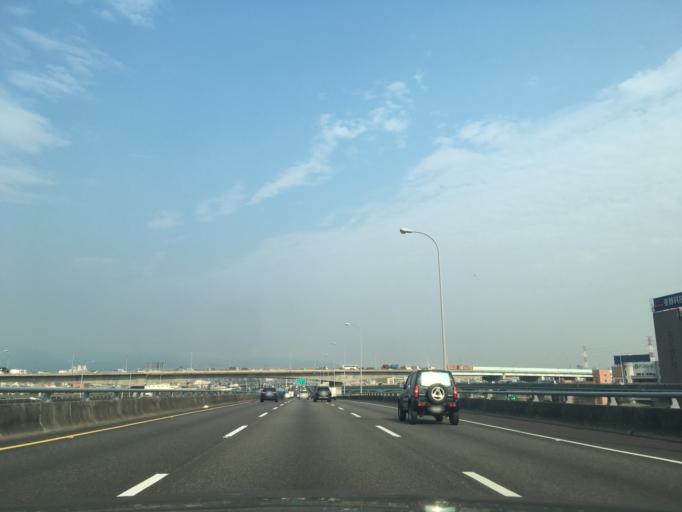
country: TW
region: Taipei
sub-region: Taipei
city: Banqiao
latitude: 25.0721
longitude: 121.4507
